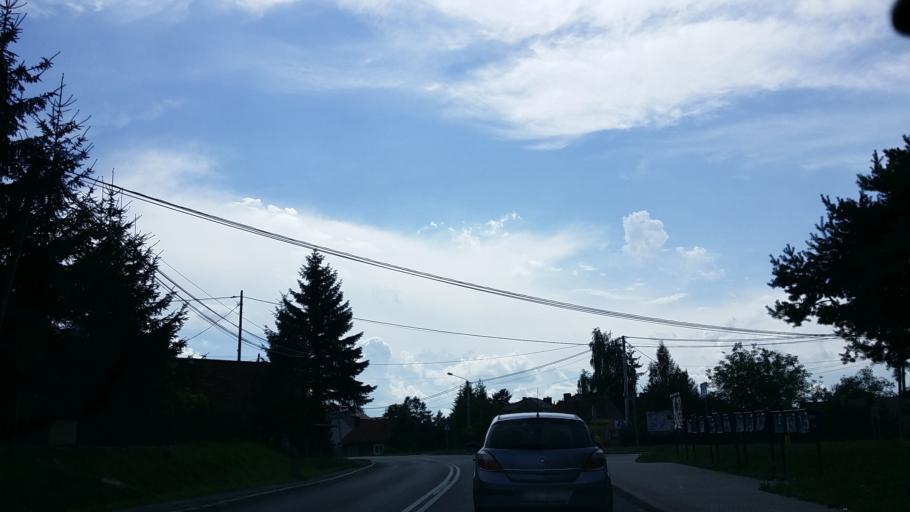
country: PL
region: Lesser Poland Voivodeship
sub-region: Powiat wielicki
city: Wieliczka
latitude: 49.9716
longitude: 20.0606
